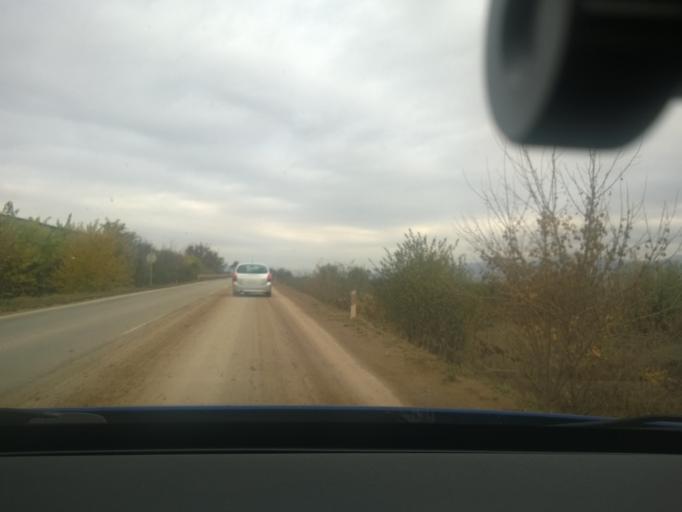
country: RS
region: Central Serbia
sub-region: Pirotski Okrug
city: Pirot
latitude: 43.0724
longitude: 22.6712
